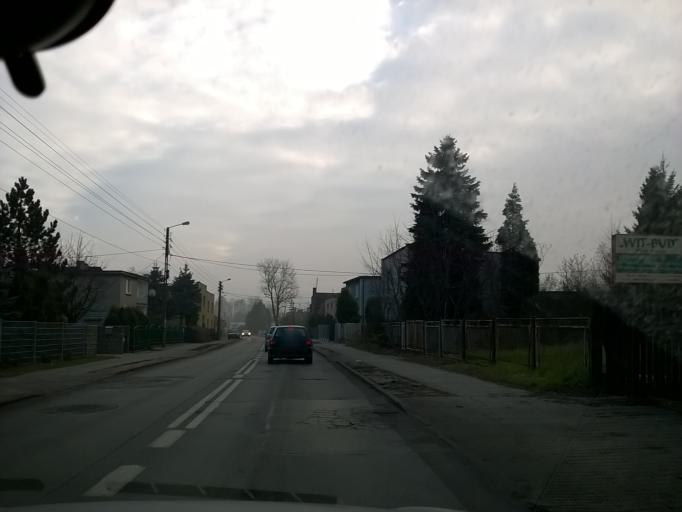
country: PL
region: Silesian Voivodeship
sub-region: Ruda Slaska
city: Ruda Slaska
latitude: 50.2484
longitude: 18.8366
